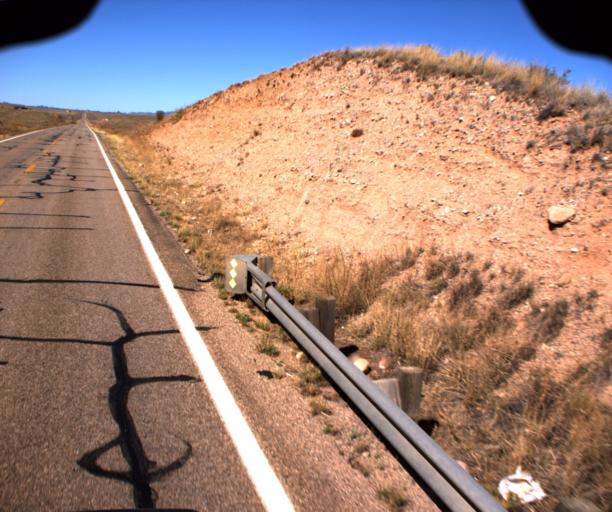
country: US
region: Arizona
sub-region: Cochise County
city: Huachuca City
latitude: 31.7035
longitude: -110.5869
